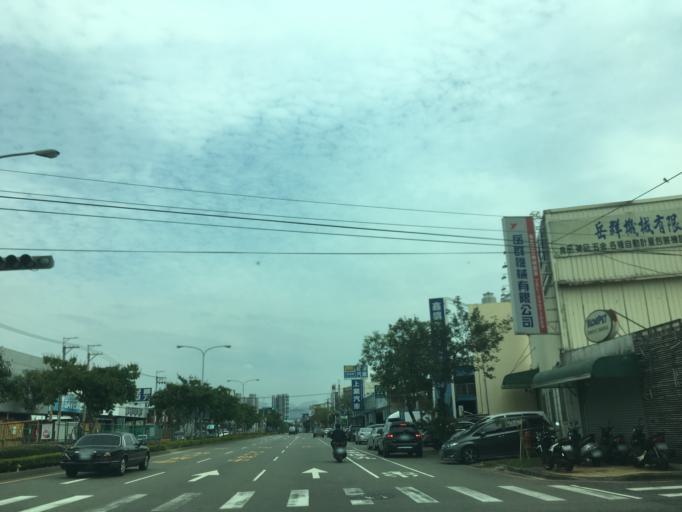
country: TW
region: Taiwan
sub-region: Taichung City
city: Taichung
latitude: 24.1061
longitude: 120.6658
